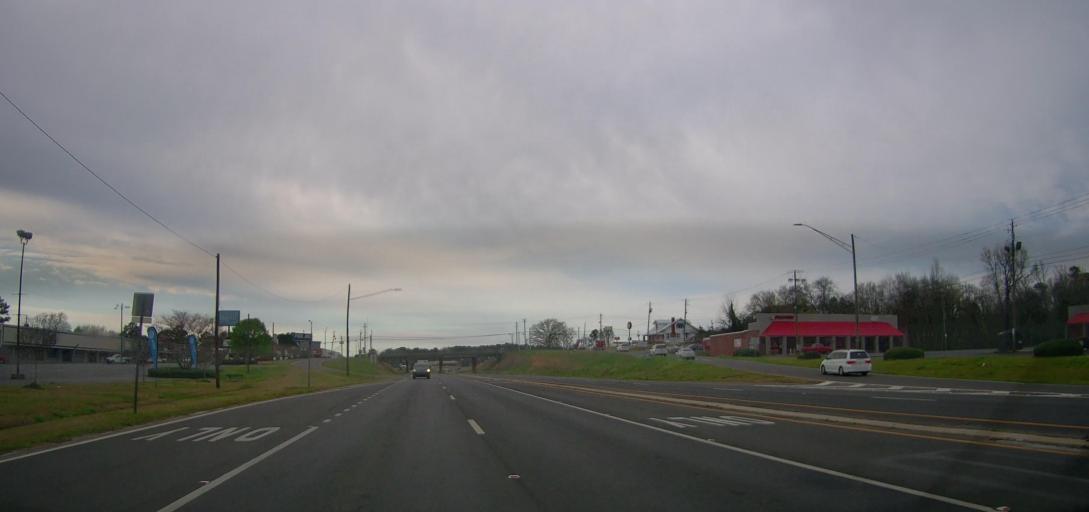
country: US
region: Alabama
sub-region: Walker County
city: Jasper
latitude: 33.8488
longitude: -87.2833
